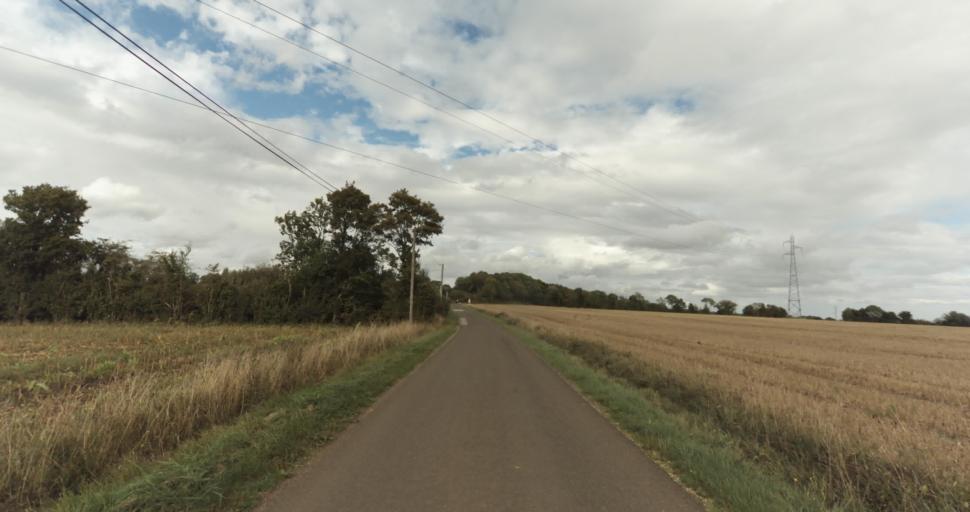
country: FR
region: Lower Normandy
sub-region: Departement de l'Orne
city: Sainte-Gauburge-Sainte-Colombe
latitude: 48.7467
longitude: 0.3760
